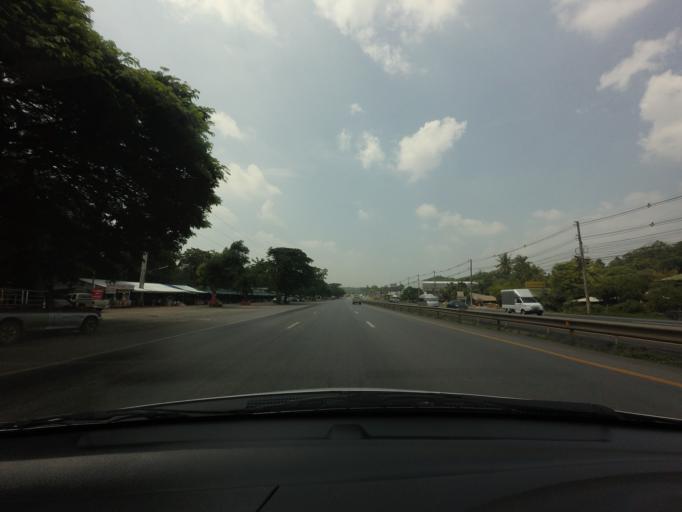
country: TH
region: Nakhon Ratchasima
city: Pak Chong
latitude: 14.6583
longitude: 101.3799
